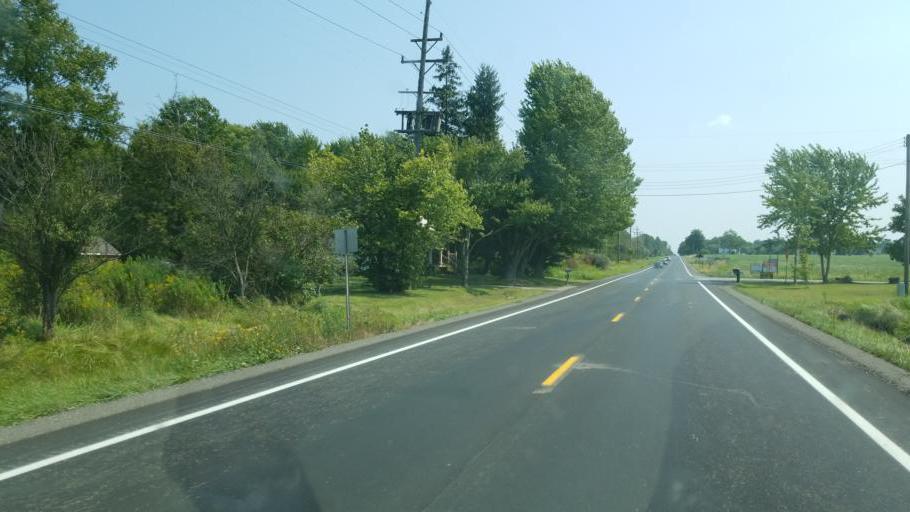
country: US
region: Ohio
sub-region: Ashtabula County
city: Orwell
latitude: 41.5350
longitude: -80.8856
